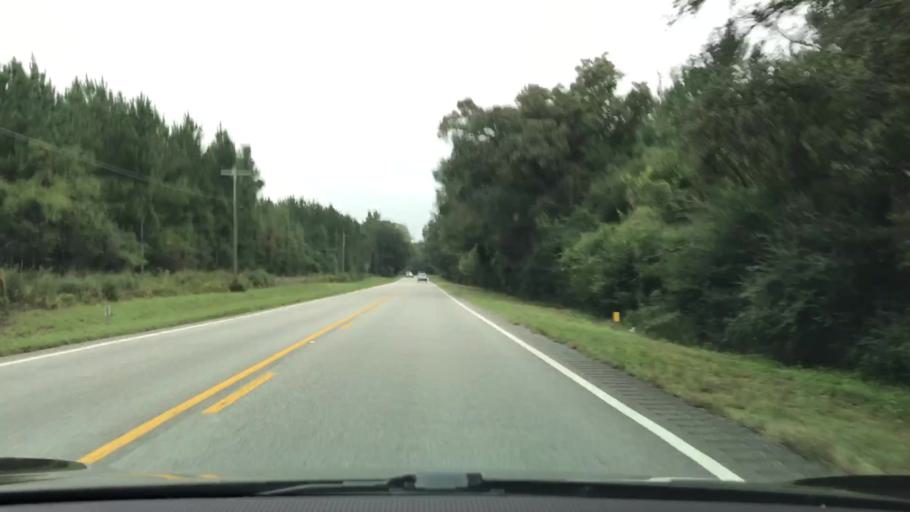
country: US
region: Alabama
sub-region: Coffee County
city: Elba
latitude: 31.4683
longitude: -86.0643
